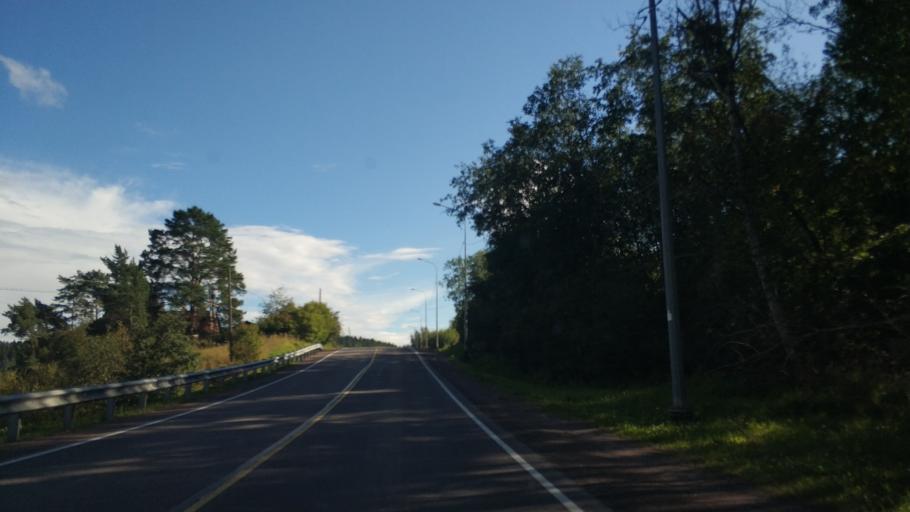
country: RU
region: Republic of Karelia
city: Sortavala
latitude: 61.6648
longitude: 30.6544
